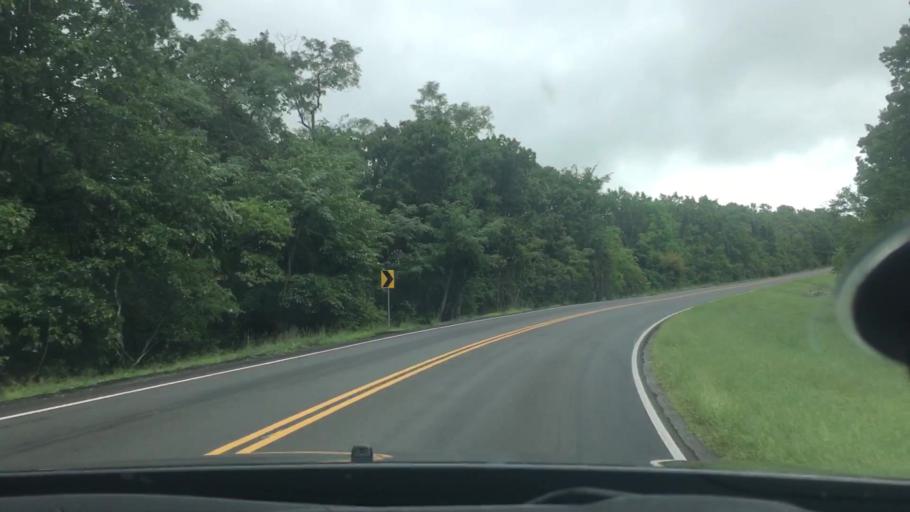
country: US
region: Oklahoma
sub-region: Sequoyah County
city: Vian
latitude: 35.6580
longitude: -94.9517
